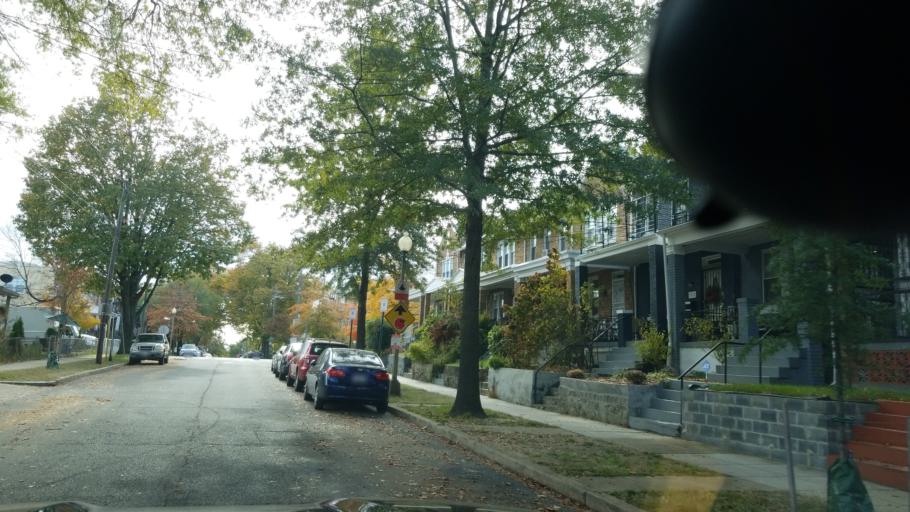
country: US
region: Maryland
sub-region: Montgomery County
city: Takoma Park
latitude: 38.9591
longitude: -77.0242
